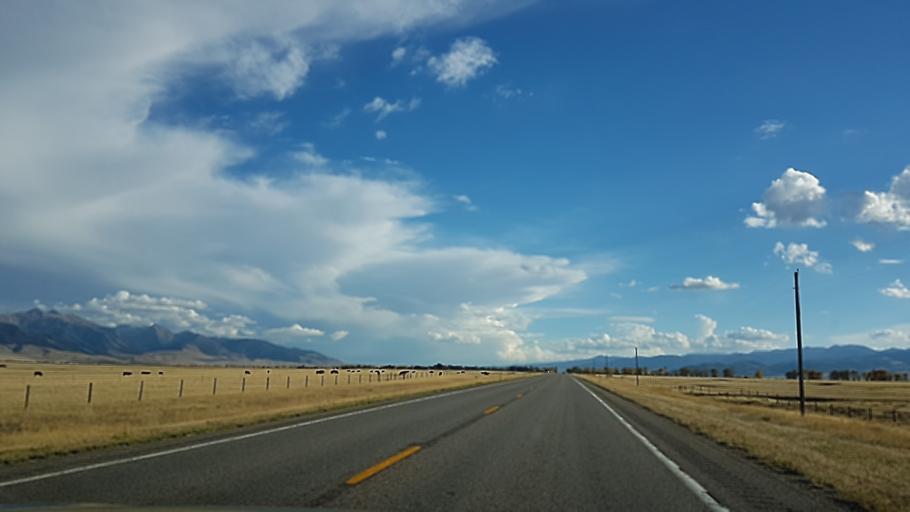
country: US
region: Montana
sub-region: Madison County
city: Virginia City
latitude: 45.2216
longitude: -111.6789
